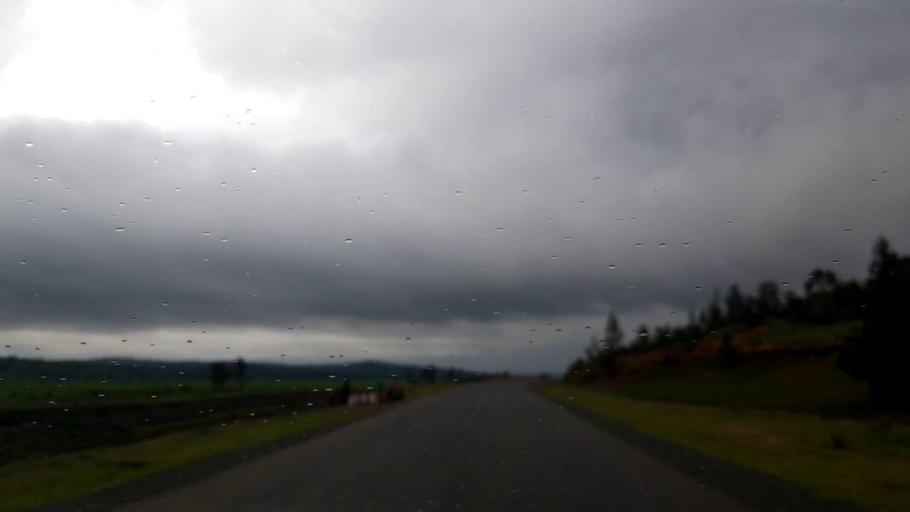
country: RW
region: Northern Province
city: Byumba
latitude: -1.4457
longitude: 30.2499
